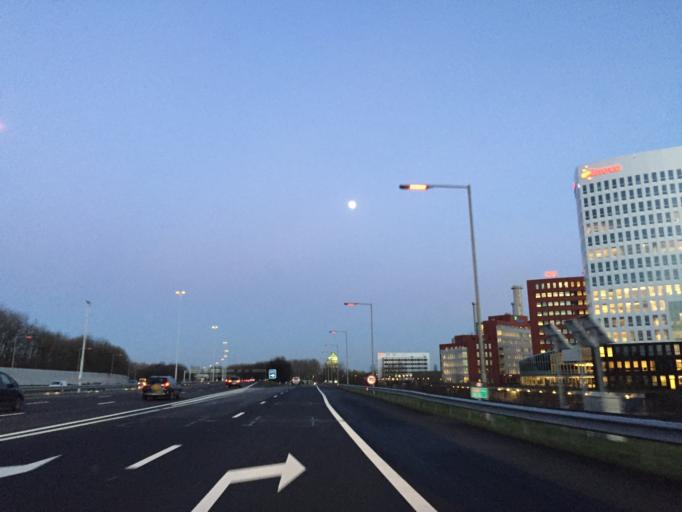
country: NL
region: South Holland
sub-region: Gemeente Rotterdam
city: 's-Gravenland
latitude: 51.9540
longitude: 4.5555
